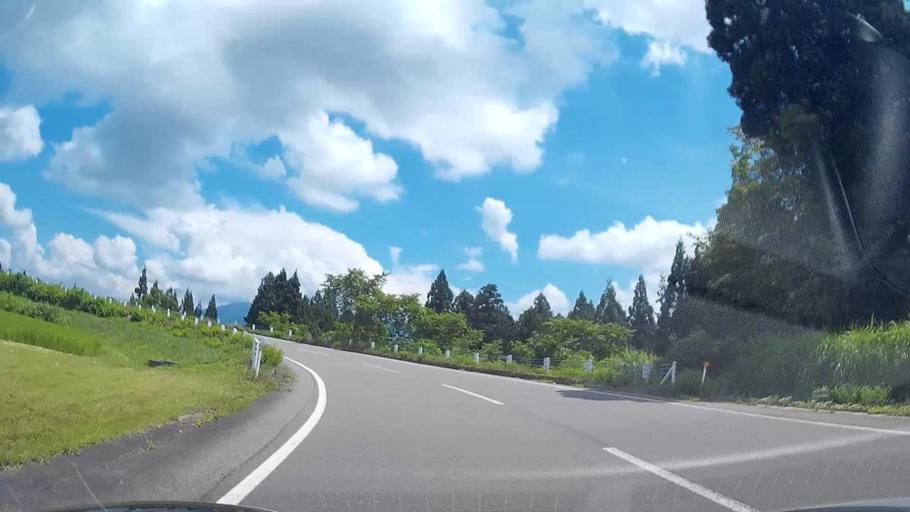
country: JP
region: Niigata
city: Shiozawa
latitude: 37.0216
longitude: 138.8052
